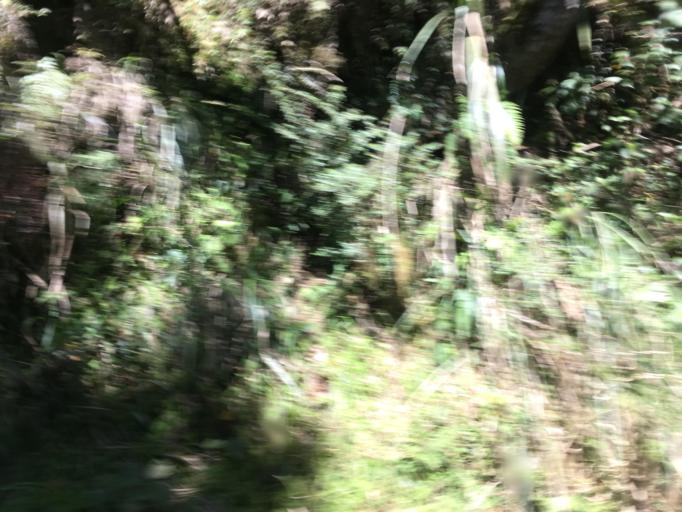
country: TW
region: Taiwan
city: Daxi
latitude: 24.6064
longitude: 121.4580
